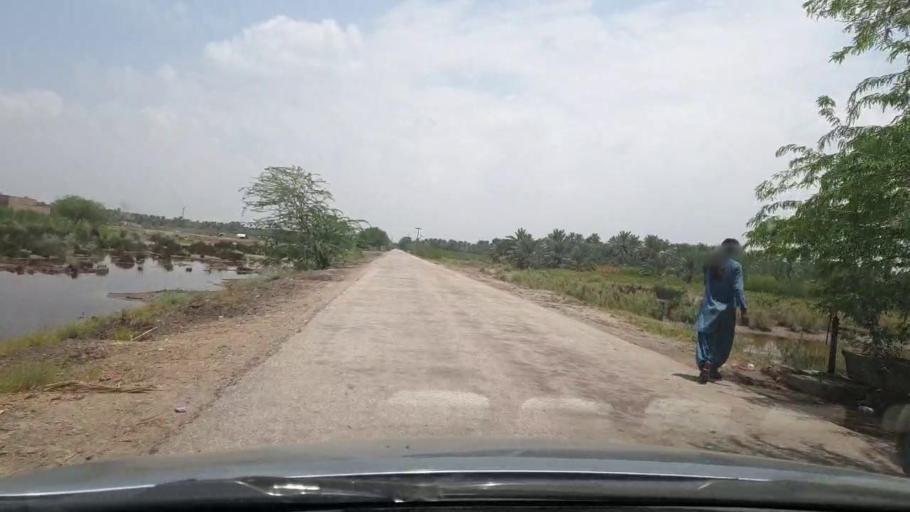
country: PK
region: Sindh
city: Khairpur
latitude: 27.4385
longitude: 68.7511
